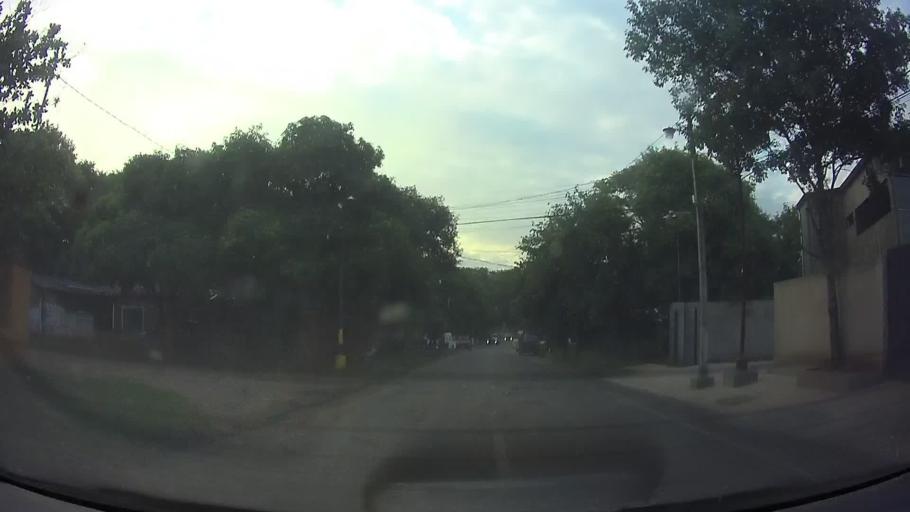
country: PY
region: Central
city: San Lorenzo
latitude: -25.2614
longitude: -57.4947
